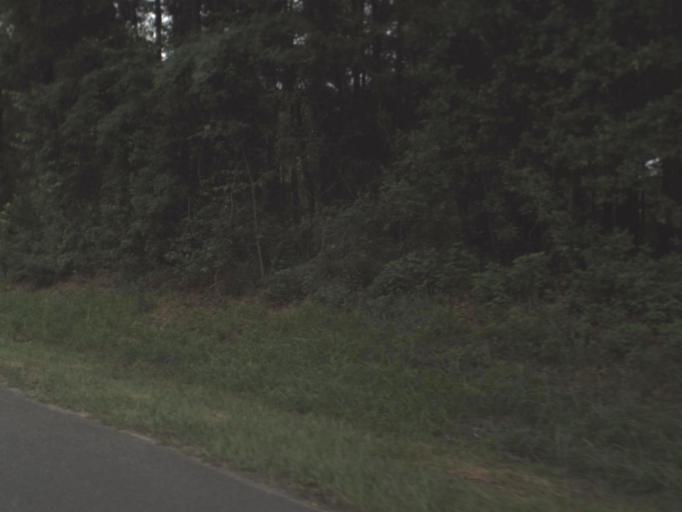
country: US
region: Florida
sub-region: Alachua County
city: Archer
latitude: 29.5437
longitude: -82.5221
